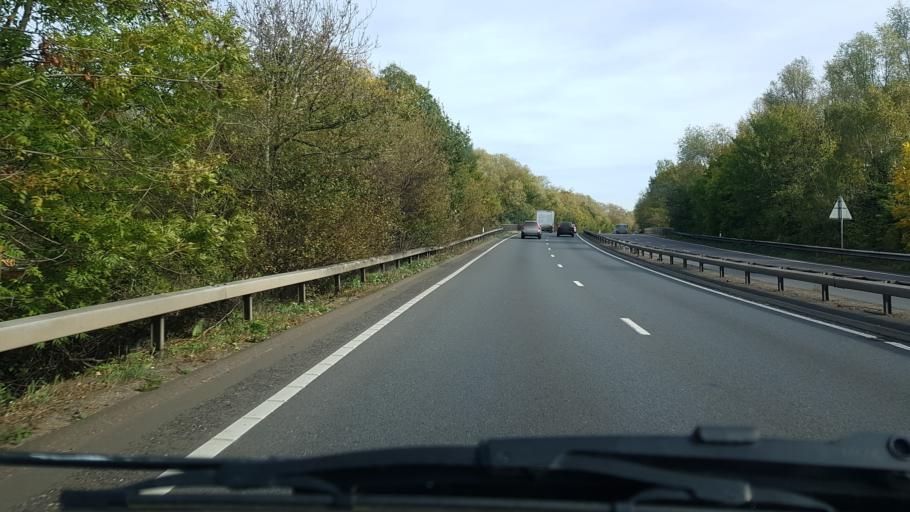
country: GB
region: England
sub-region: Surrey
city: Guildford
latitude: 51.2488
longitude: -0.5838
